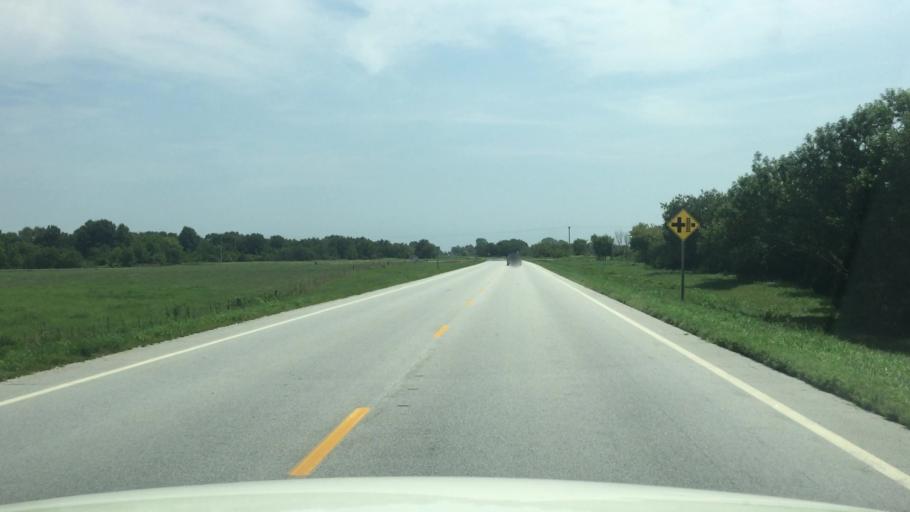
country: US
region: Kansas
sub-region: Cherokee County
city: Columbus
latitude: 37.1796
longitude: -94.9623
